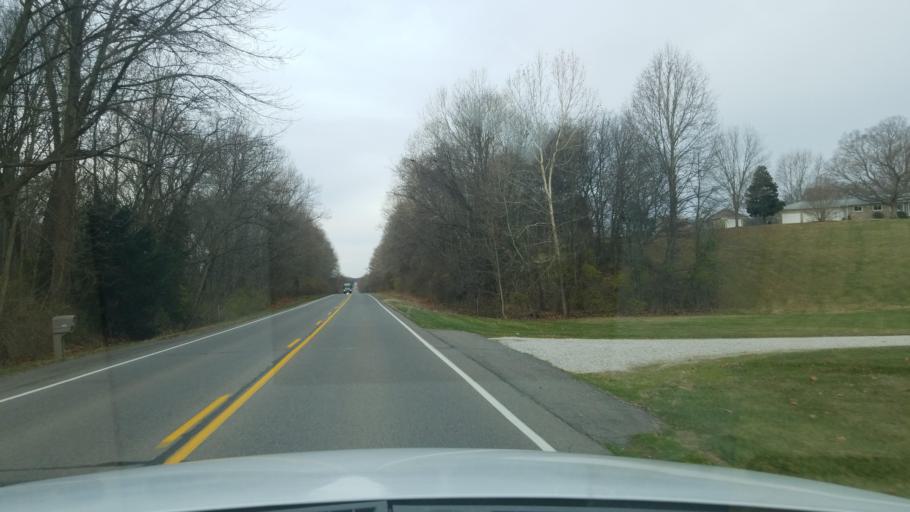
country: US
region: Indiana
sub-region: Posey County
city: Mount Vernon
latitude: 37.9291
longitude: -87.9553
